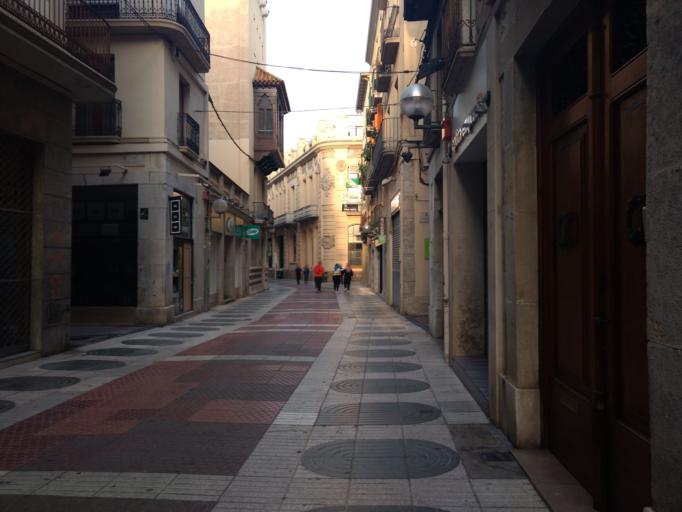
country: ES
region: Catalonia
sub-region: Provincia de Girona
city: Figueres
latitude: 42.2678
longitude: 2.9618
